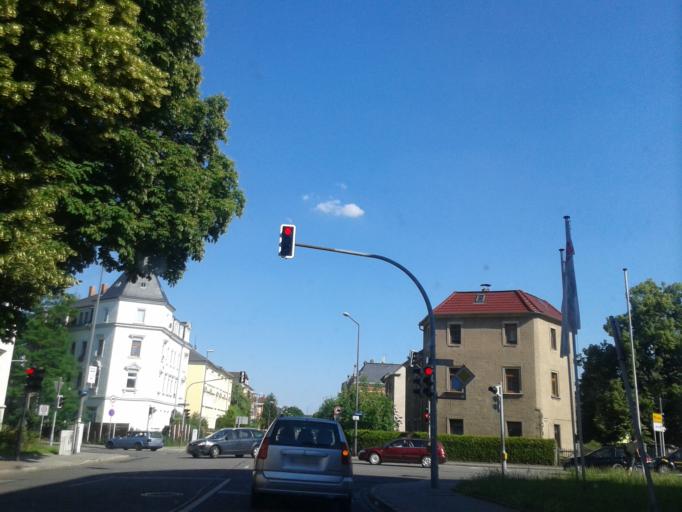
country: DE
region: Saxony
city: Radebeul
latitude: 51.0880
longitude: 13.6984
